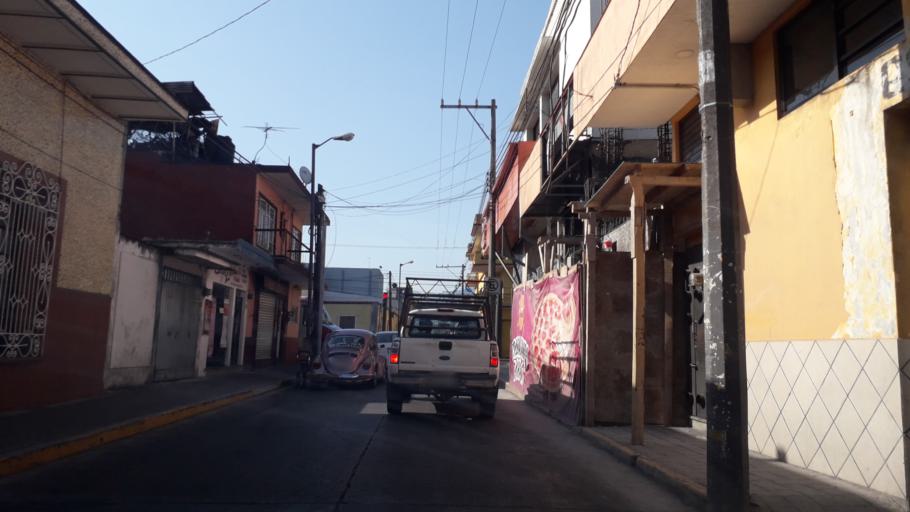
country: MX
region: Veracruz
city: Orizaba
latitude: 18.8472
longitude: -97.0978
